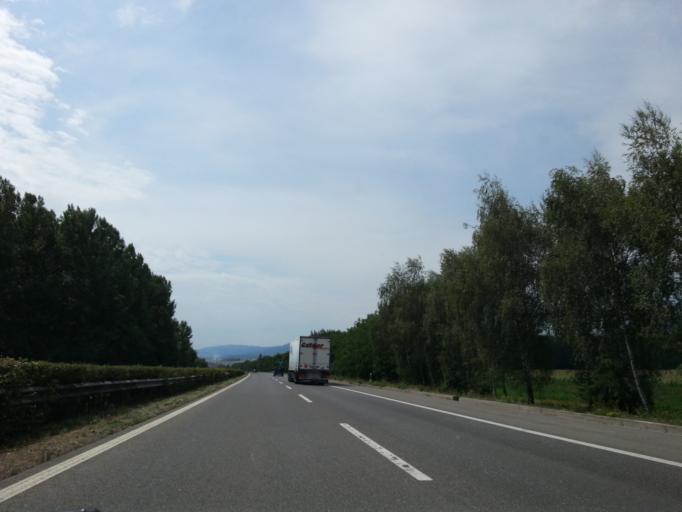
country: CH
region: Vaud
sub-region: Jura-Nord vaudois District
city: Chavornay
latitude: 46.7431
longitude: 6.5910
